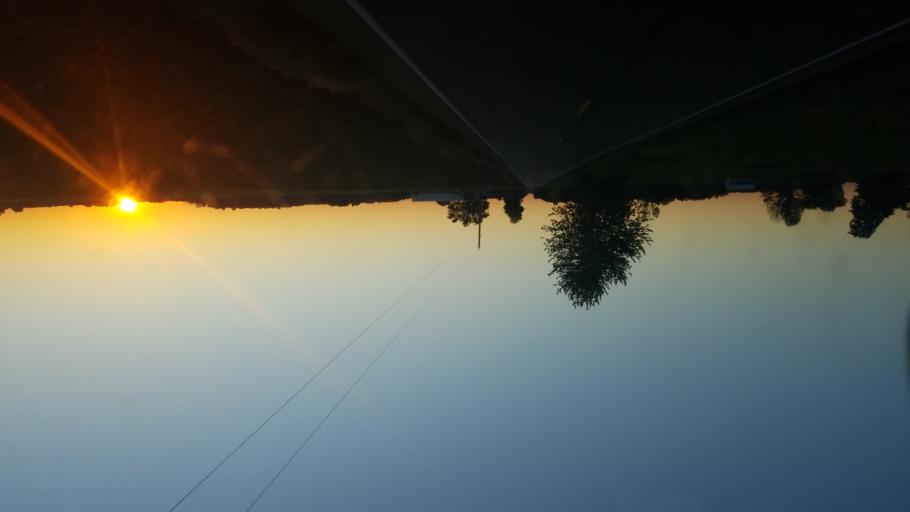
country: US
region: Indiana
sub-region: Elkhart County
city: Nappanee
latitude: 41.3614
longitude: -85.9862
